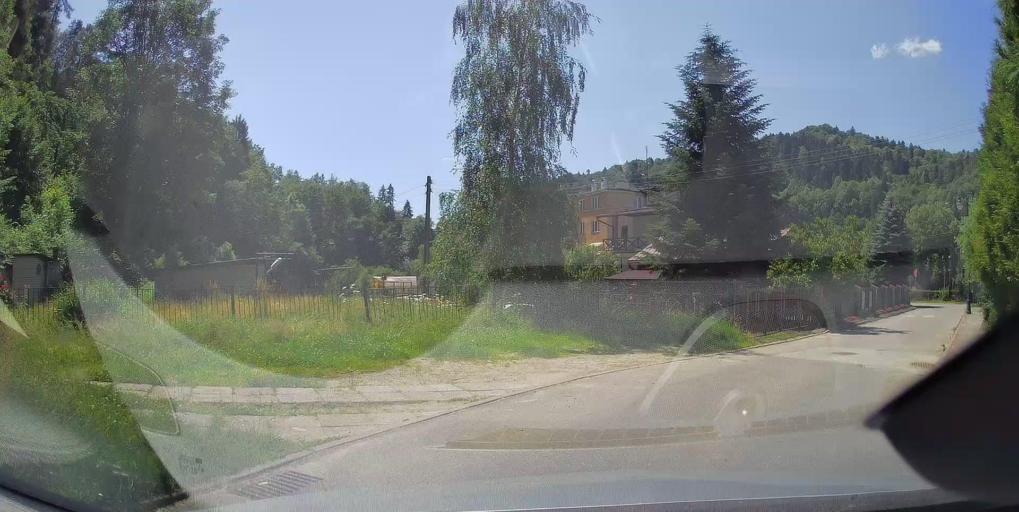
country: PL
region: Lesser Poland Voivodeship
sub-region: Powiat nowosadecki
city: Muszyna
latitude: 49.3564
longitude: 20.8903
